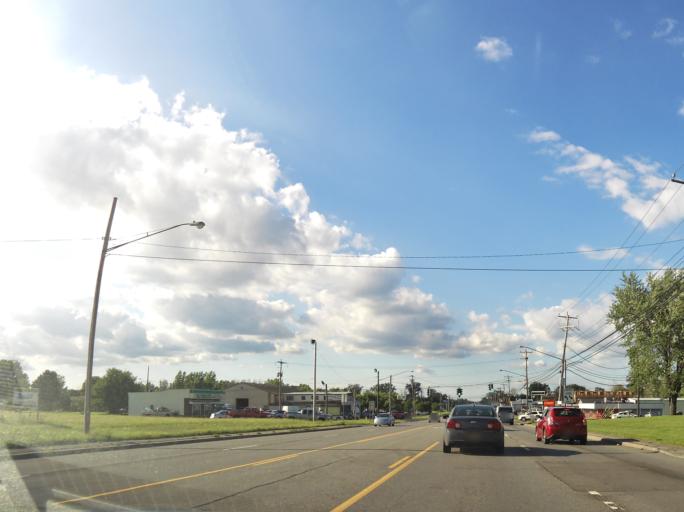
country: US
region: New York
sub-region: Erie County
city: Depew
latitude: 42.9334
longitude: -78.6969
